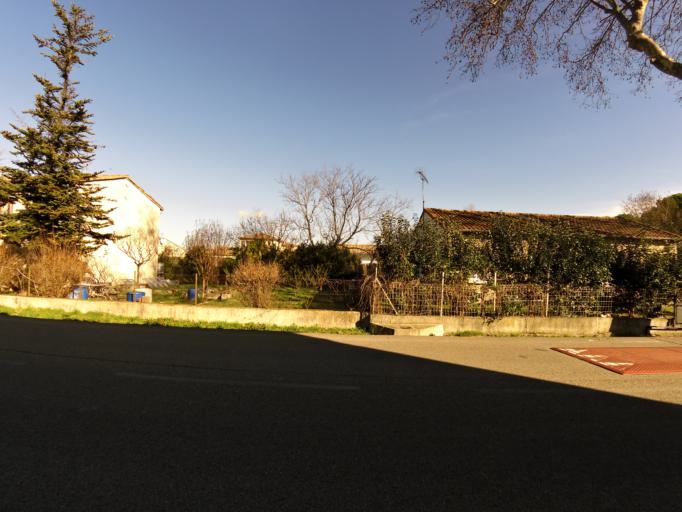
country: FR
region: Languedoc-Roussillon
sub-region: Departement de l'Herault
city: Saint-Martin-de-Londres
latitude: 43.7869
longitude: 3.7339
